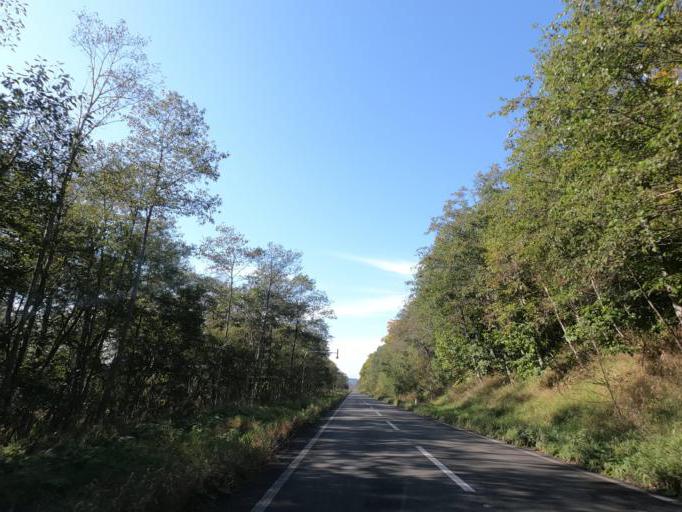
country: JP
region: Hokkaido
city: Obihiro
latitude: 42.6263
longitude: 143.5326
